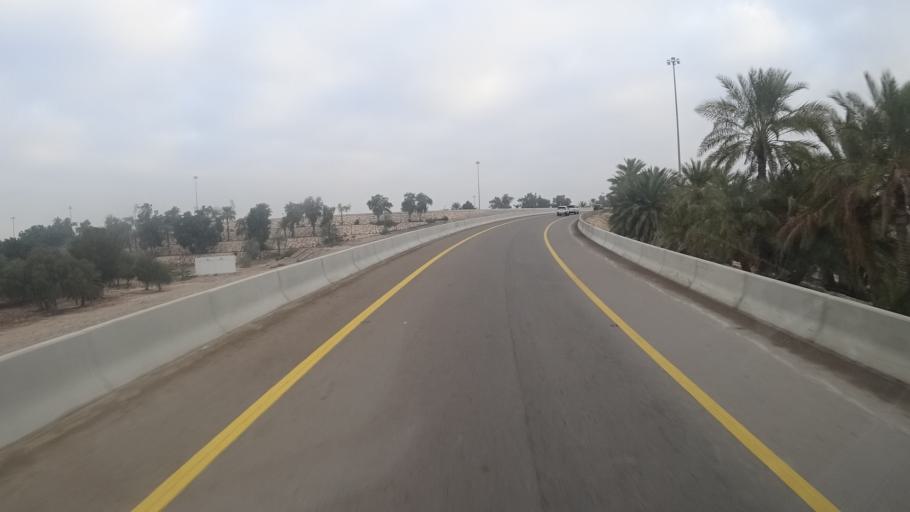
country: AE
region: Abu Dhabi
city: Abu Dhabi
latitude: 24.3885
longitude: 54.5432
